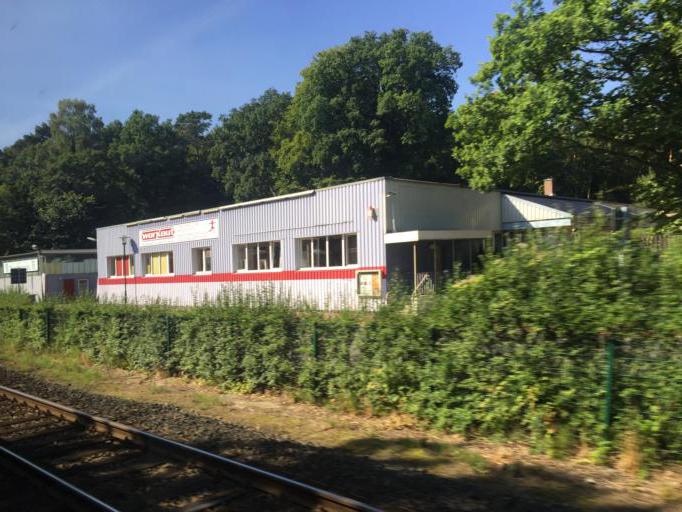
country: DE
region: Schleswig-Holstein
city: Bad Schwartau
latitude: 53.9191
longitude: 10.7059
